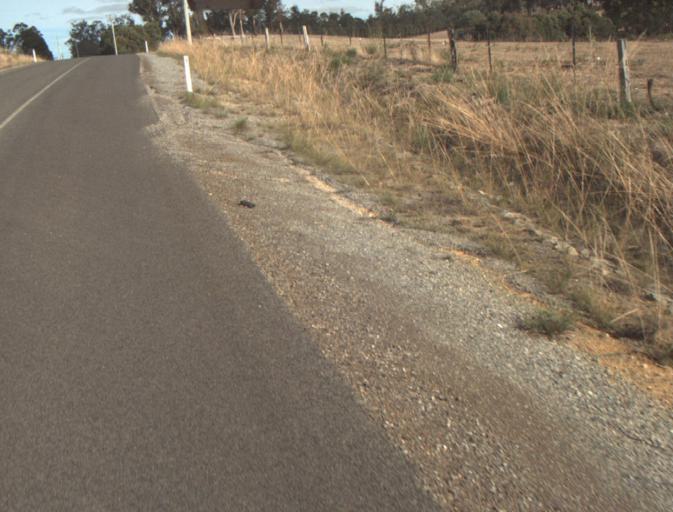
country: AU
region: Tasmania
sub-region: Launceston
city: Mayfield
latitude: -41.2116
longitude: 147.1338
